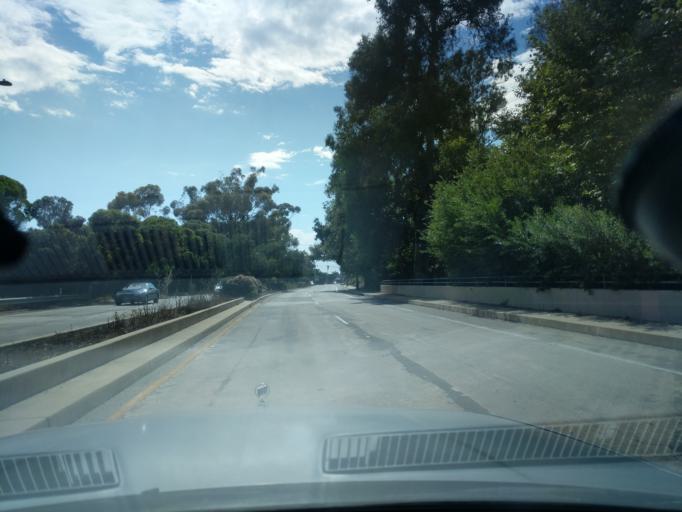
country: US
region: California
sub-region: Santa Barbara County
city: Goleta
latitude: 34.4414
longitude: -119.8172
